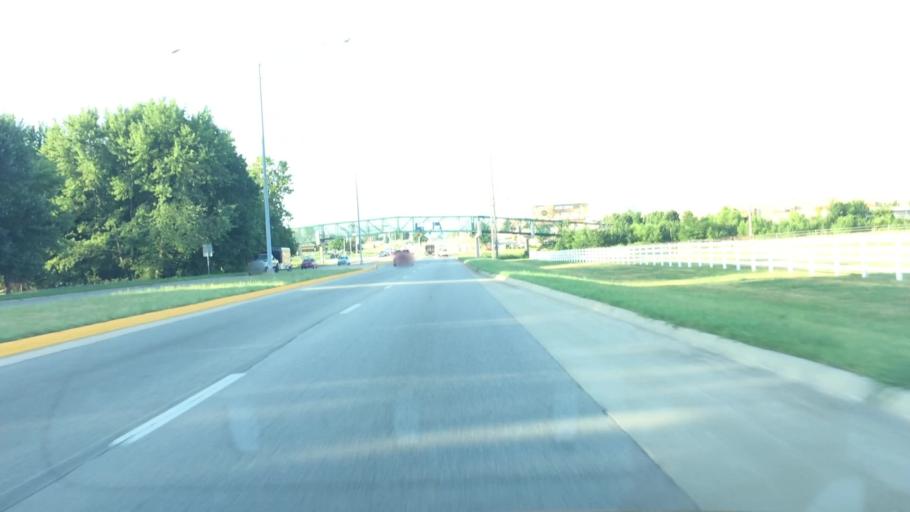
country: US
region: Missouri
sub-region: Greene County
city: Springfield
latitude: 37.1693
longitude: -93.3162
